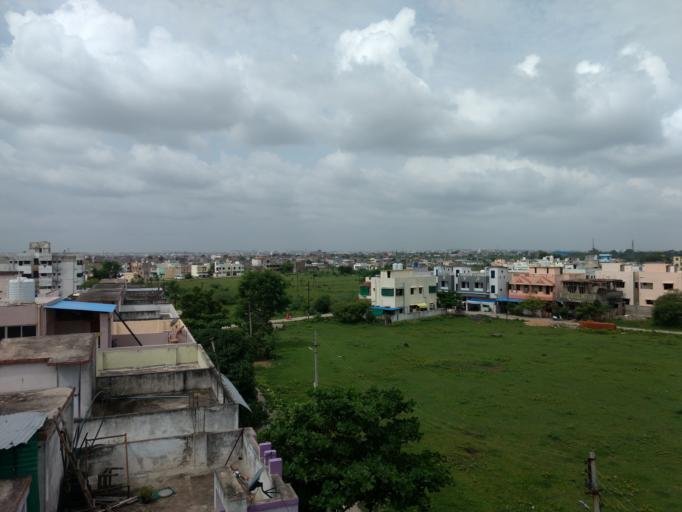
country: IN
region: Maharashtra
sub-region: Nagpur Division
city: Kamthi
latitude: 21.1945
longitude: 79.1425
